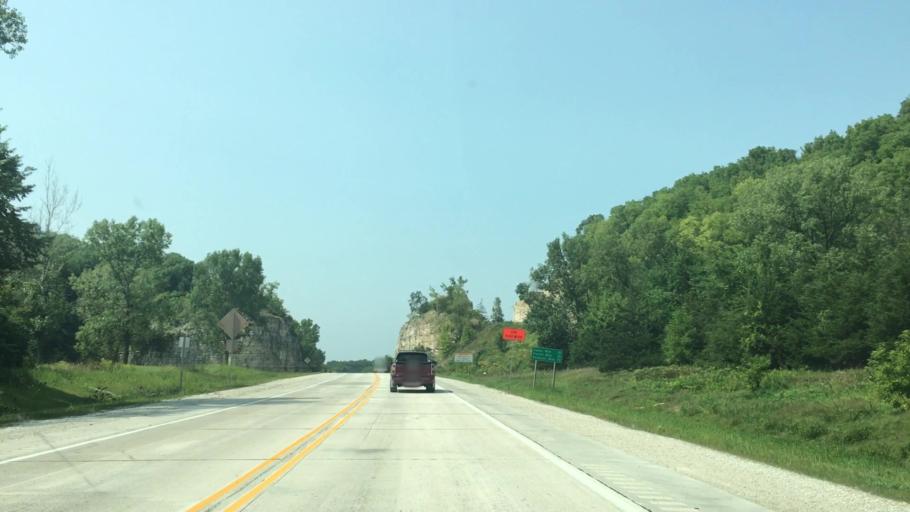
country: US
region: Iowa
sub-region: Winneshiek County
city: Decorah
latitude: 43.2936
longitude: -91.8067
